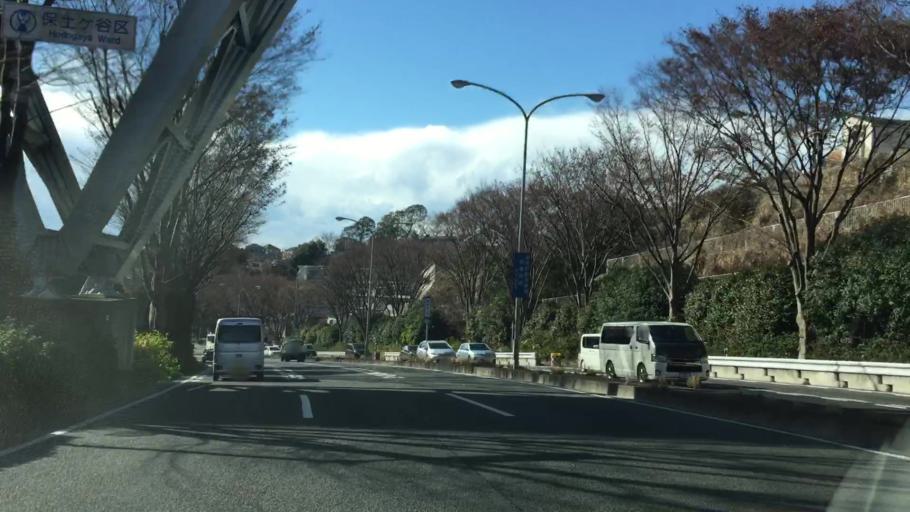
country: JP
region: Kanagawa
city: Yokohama
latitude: 35.4789
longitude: 139.5786
